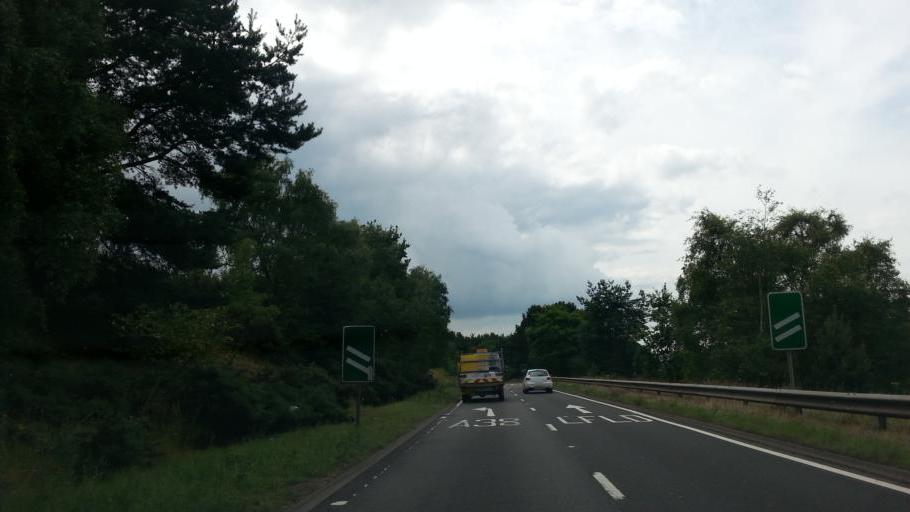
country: GB
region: England
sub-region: Staffordshire
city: Lichfield
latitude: 52.6648
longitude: -1.8138
